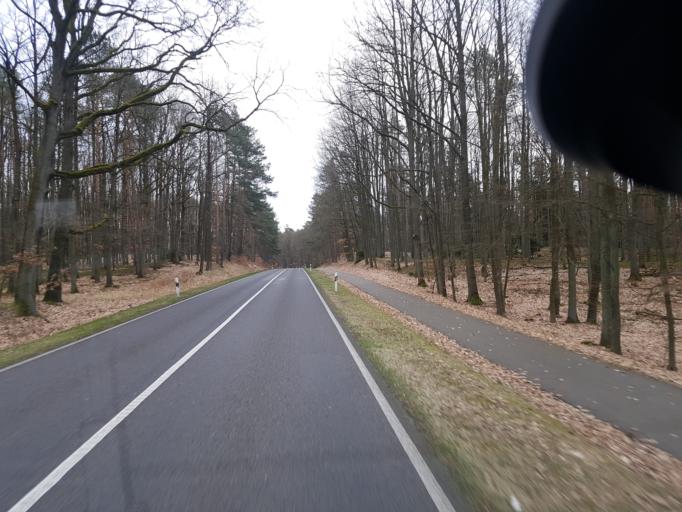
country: DE
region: Brandenburg
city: Gross Lindow
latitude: 52.1740
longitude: 14.4842
